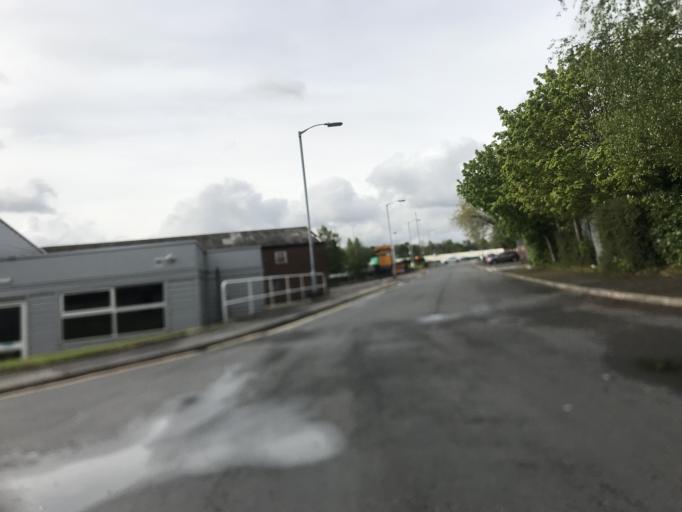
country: GB
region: England
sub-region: Borough of Stockport
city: Cheadle Heath
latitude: 53.4110
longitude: -2.1756
